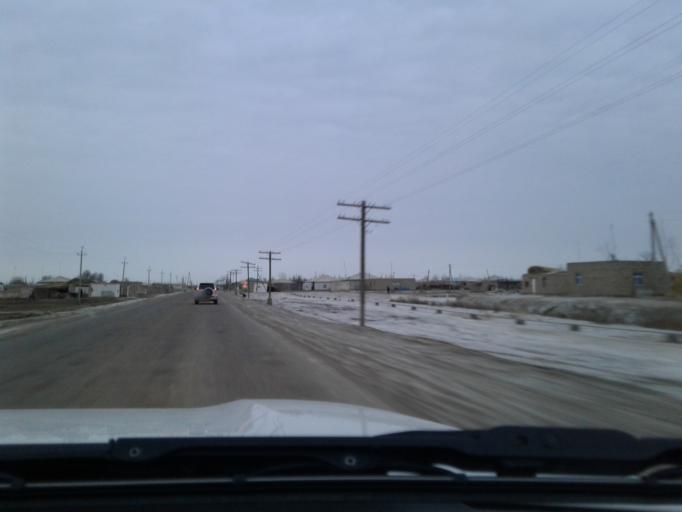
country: TM
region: Dasoguz
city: Dasoguz
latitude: 42.0059
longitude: 59.8816
